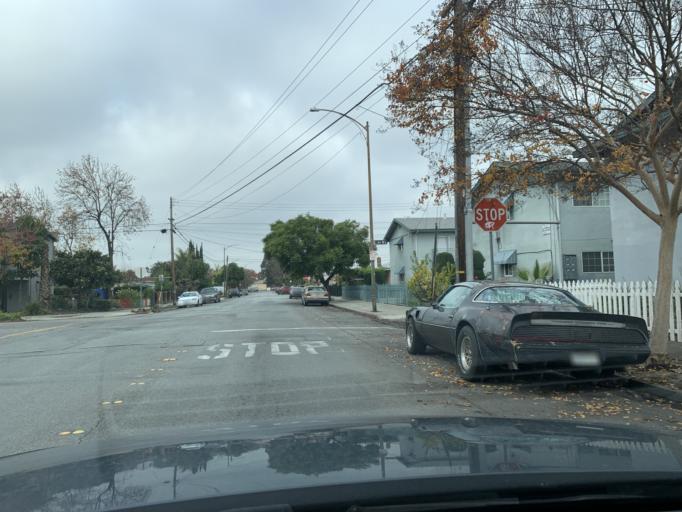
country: US
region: California
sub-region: Santa Clara County
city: Alum Rock
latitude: 37.3432
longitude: -121.8417
